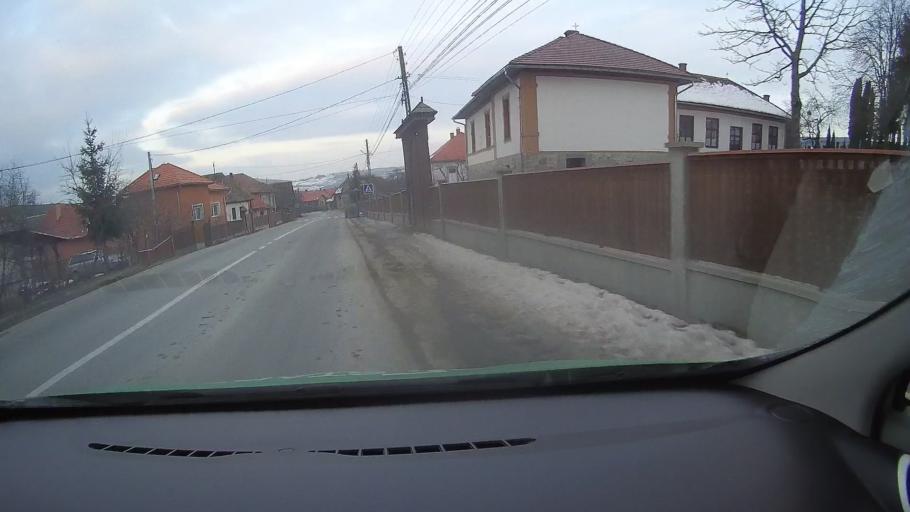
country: RO
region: Harghita
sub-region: Comuna Lupeni
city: Lupeni
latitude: 46.3563
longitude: 25.2184
